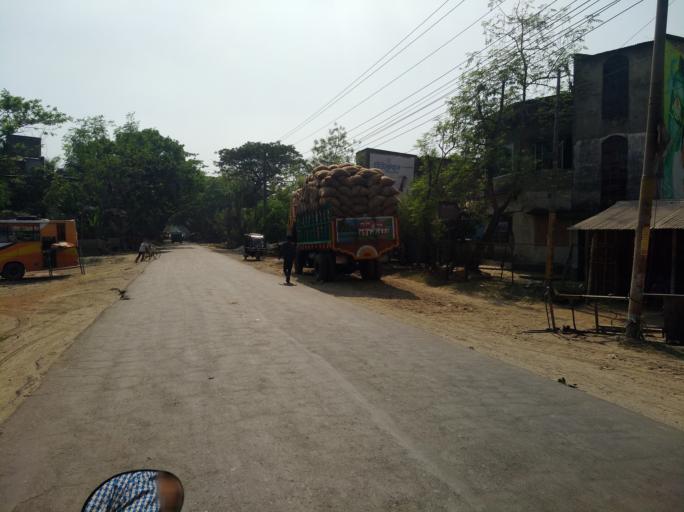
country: BD
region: Khulna
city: Kaliganj
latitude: 23.5518
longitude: 89.1714
